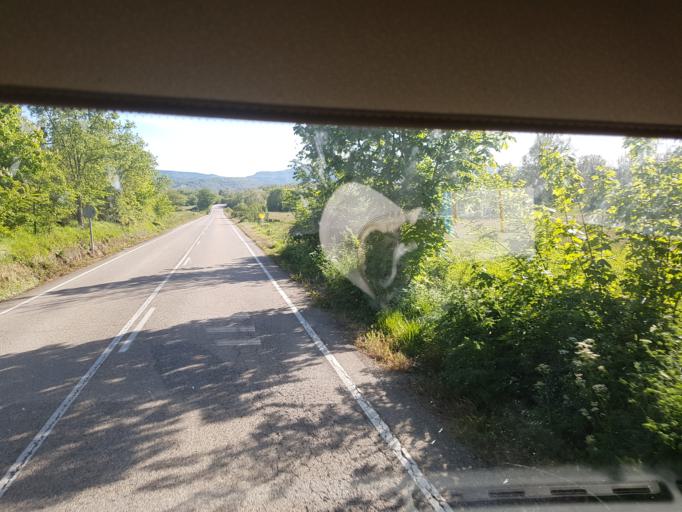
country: ES
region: Cantabria
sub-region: Provincia de Cantabria
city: San Pedro del Romeral
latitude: 42.9803
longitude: -3.7677
